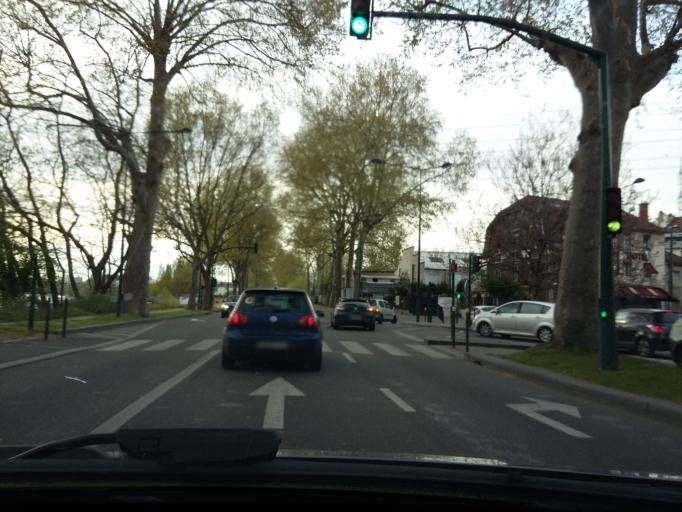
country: FR
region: Ile-de-France
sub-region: Departement de Seine-Saint-Denis
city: Villetaneuse
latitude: 48.9438
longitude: 2.3385
